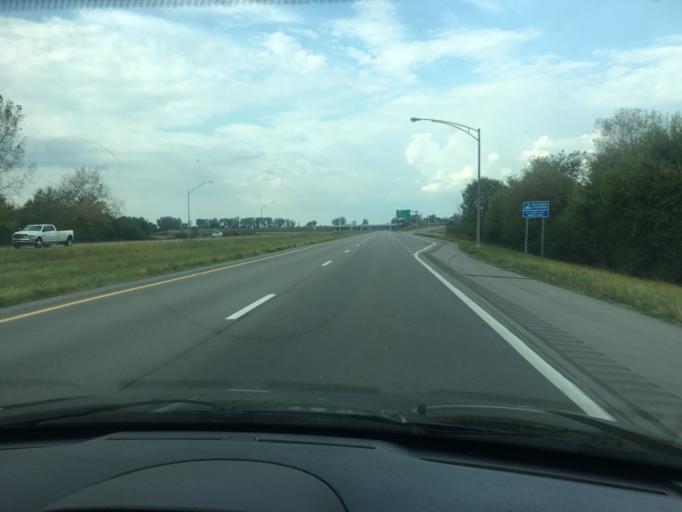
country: US
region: Ohio
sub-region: Clark County
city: Northridge
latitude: 39.9819
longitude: -83.8143
